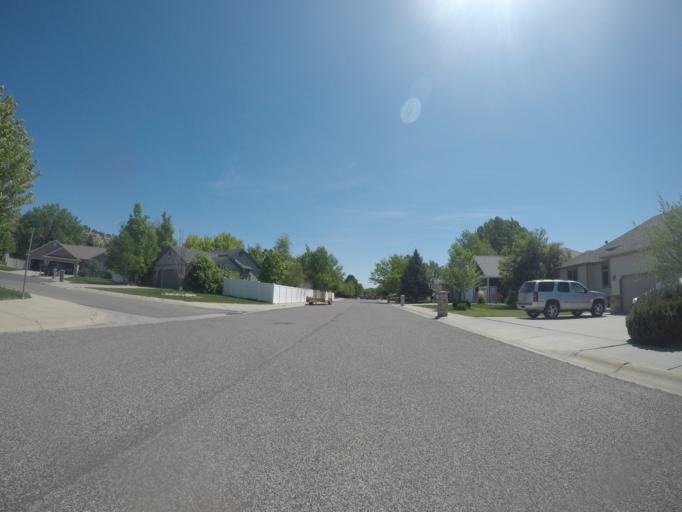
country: US
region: Montana
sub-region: Yellowstone County
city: Billings
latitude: 45.7976
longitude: -108.6093
